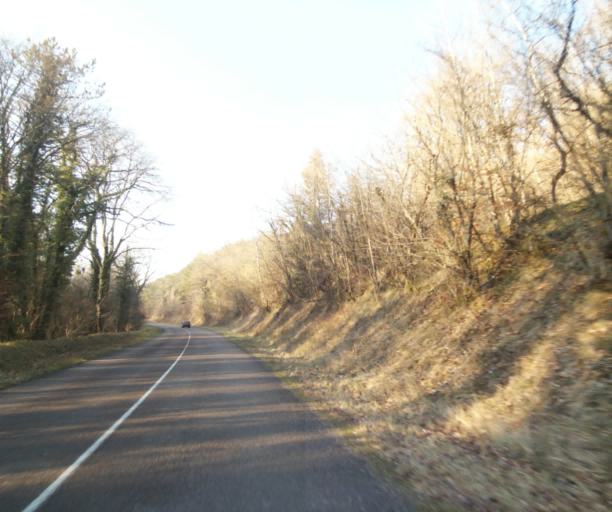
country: FR
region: Champagne-Ardenne
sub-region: Departement de la Haute-Marne
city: Bienville
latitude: 48.5641
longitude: 5.0620
